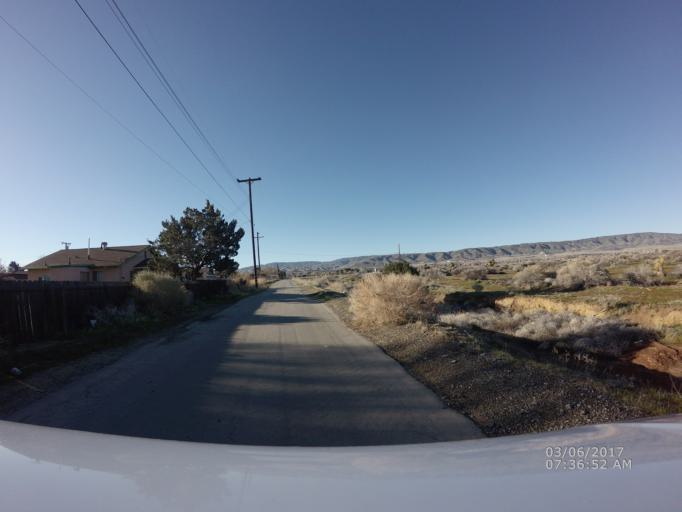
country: US
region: California
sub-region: Los Angeles County
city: Quartz Hill
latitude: 34.6661
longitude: -118.2232
